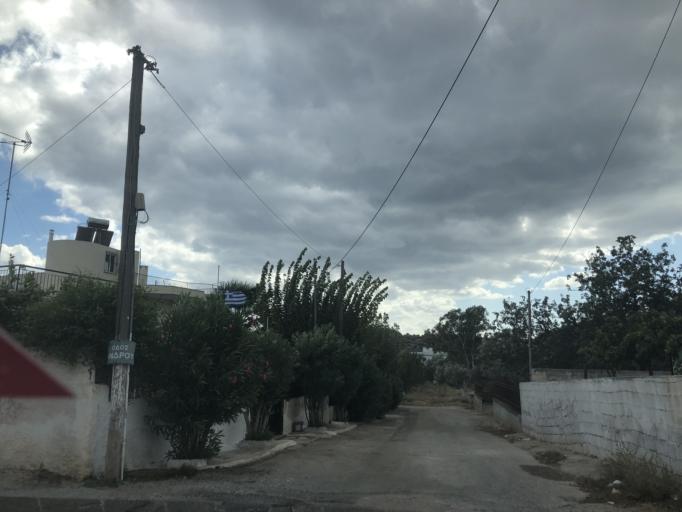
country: GR
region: Attica
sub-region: Nomarchia Anatolikis Attikis
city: Agia Marina
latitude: 37.8225
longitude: 23.8421
